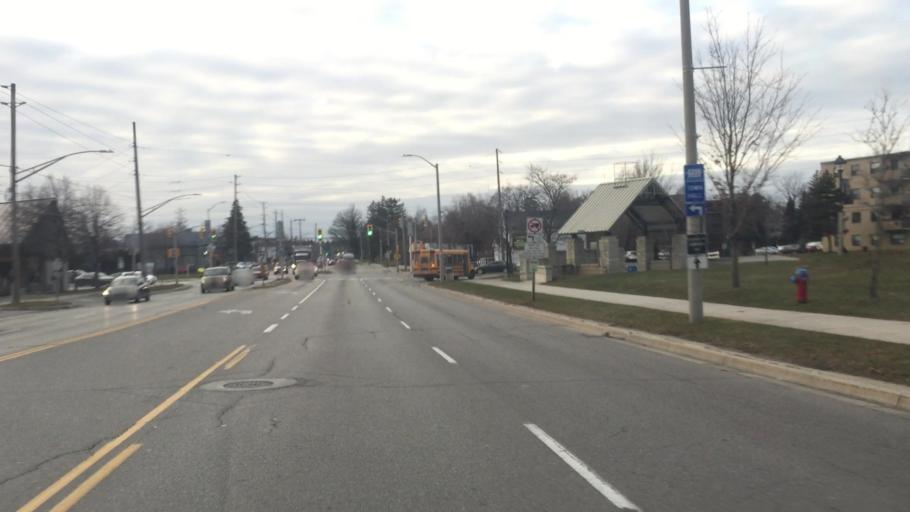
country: CA
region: Ontario
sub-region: Halton
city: Milton
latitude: 43.6509
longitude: -79.9146
